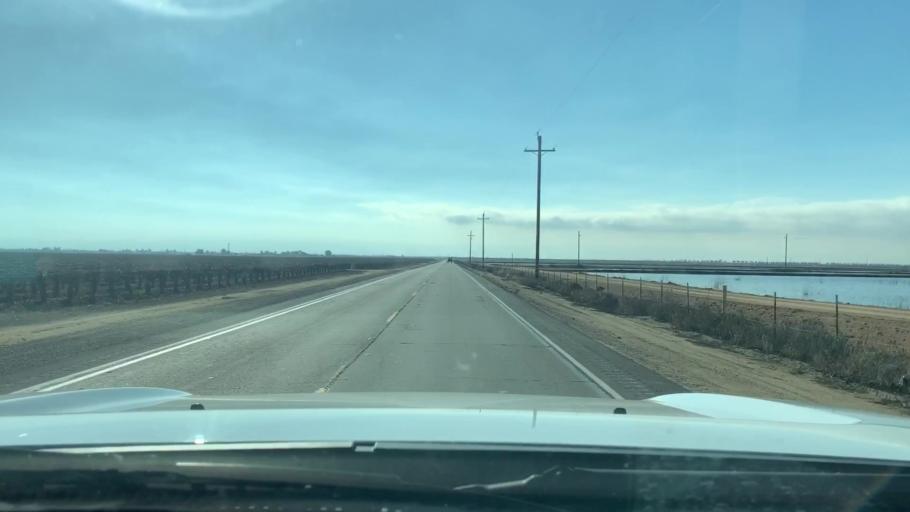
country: US
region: California
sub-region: Kern County
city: Rosedale
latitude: 35.4646
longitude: -119.1537
